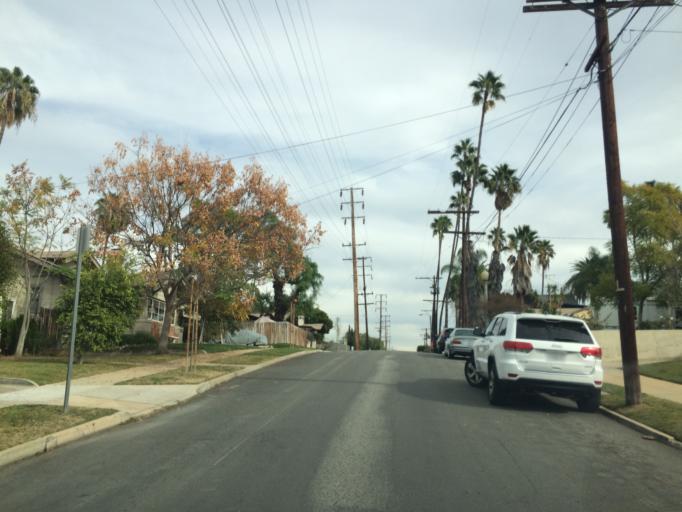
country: US
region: California
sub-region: Los Angeles County
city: South Pasadena
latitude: 34.0987
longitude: -118.1579
